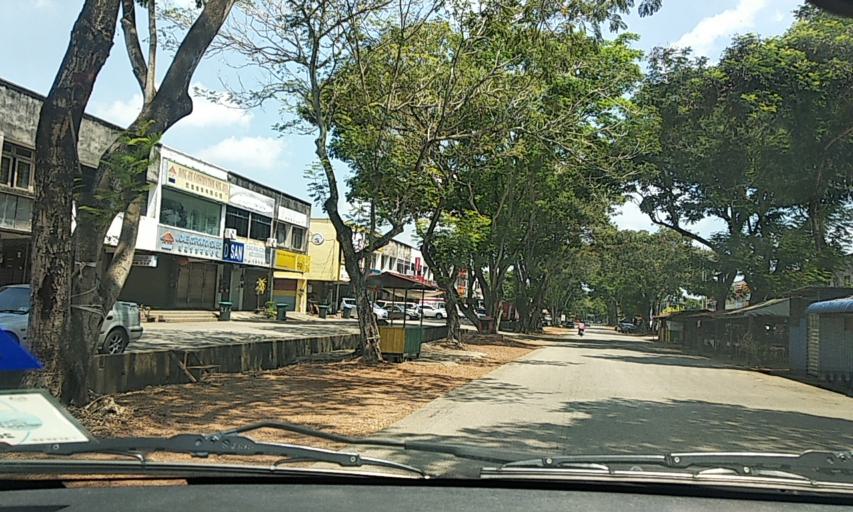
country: MY
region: Kedah
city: Sungai Petani
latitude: 5.6206
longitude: 100.4736
